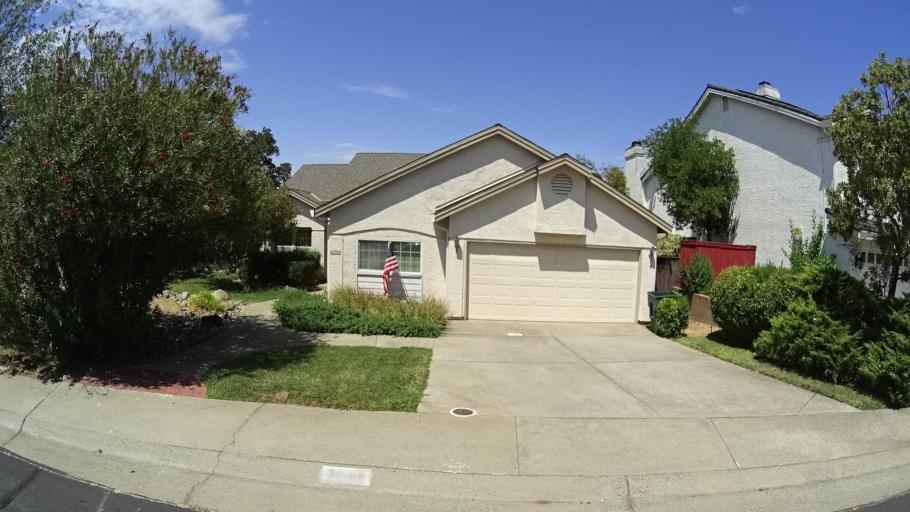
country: US
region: California
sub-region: Placer County
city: Rocklin
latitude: 38.8061
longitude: -121.2679
